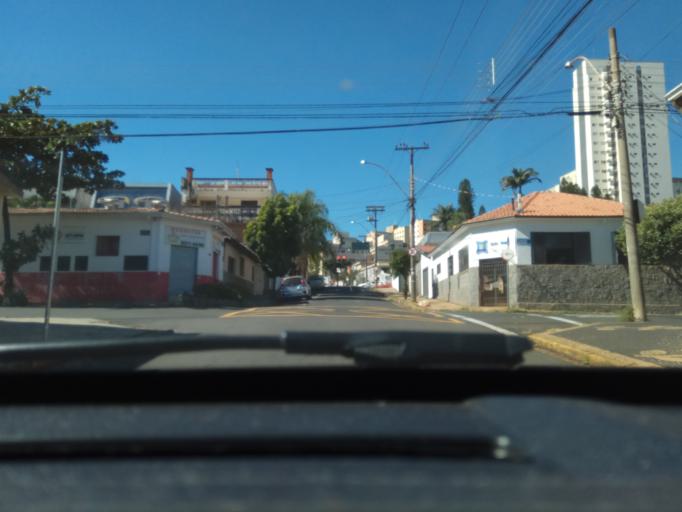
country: BR
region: Sao Paulo
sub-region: Piracicaba
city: Piracicaba
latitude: -22.7356
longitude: -47.6405
